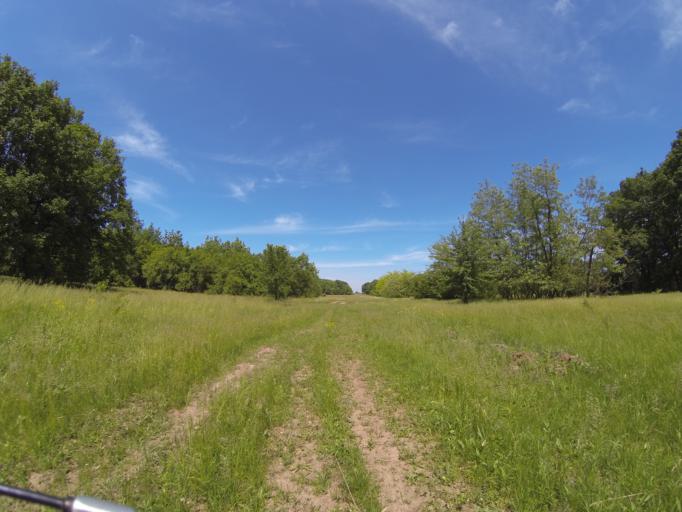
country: RO
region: Dolj
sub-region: Comuna Teslui
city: Teslui
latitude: 44.1712
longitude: 24.1662
